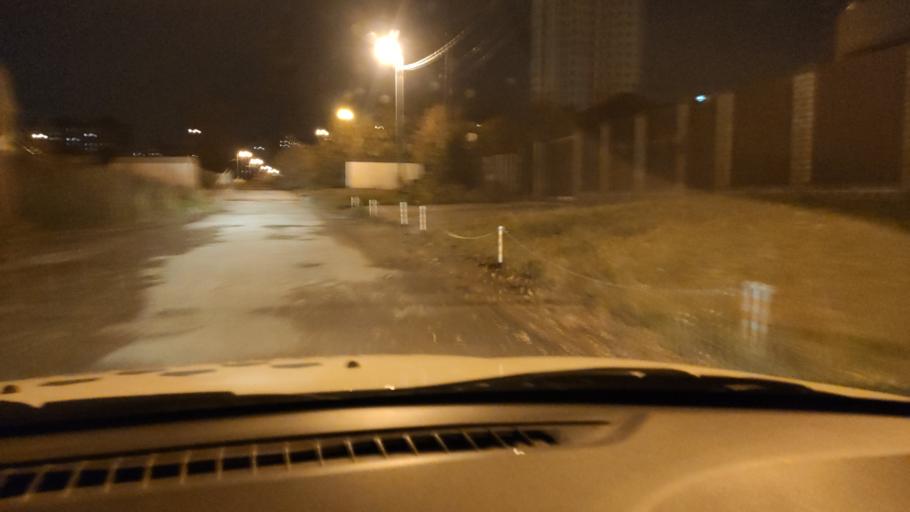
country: RU
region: Perm
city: Kondratovo
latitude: 57.9642
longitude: 56.1512
